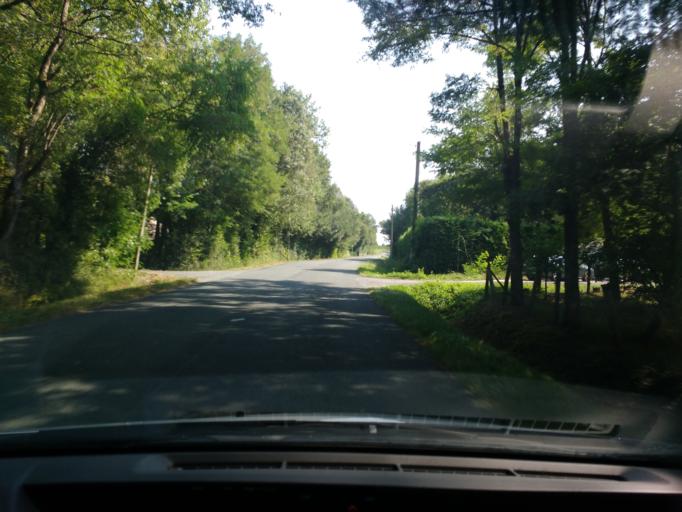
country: FR
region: Pays de la Loire
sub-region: Departement de Maine-et-Loire
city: Maze
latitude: 47.4893
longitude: -0.2810
